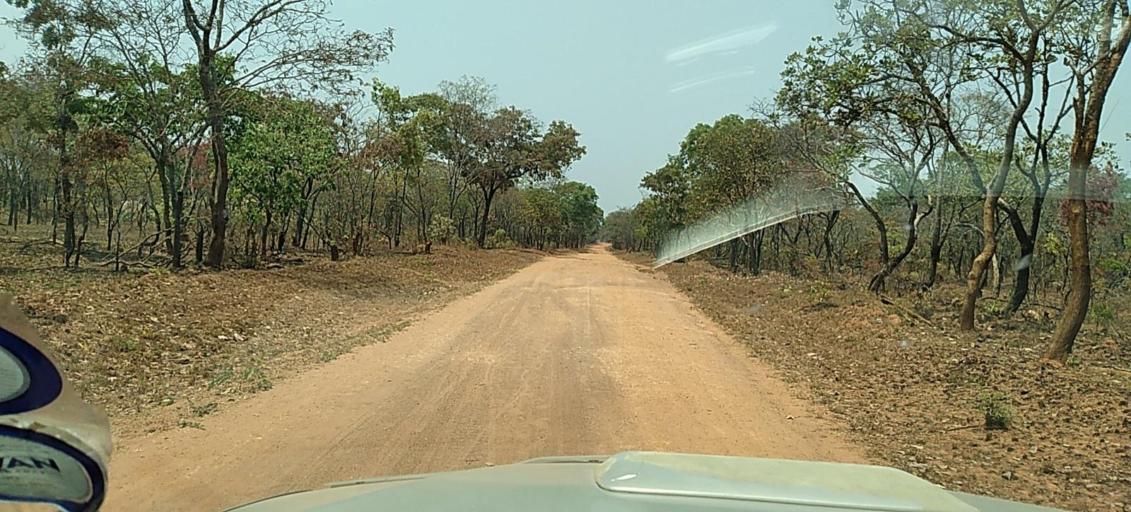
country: ZM
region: North-Western
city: Kasempa
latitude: -13.5647
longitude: 26.0921
